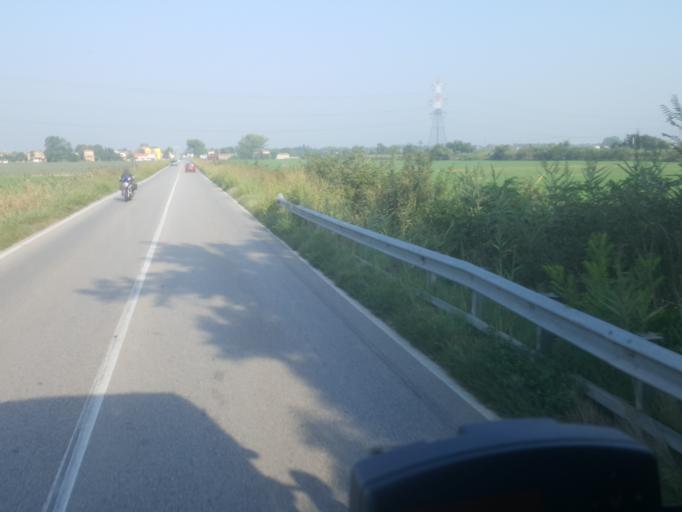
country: IT
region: Emilia-Romagna
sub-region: Provincia di Ravenna
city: Fornace Zarattini
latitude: 44.4450
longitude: 12.1320
